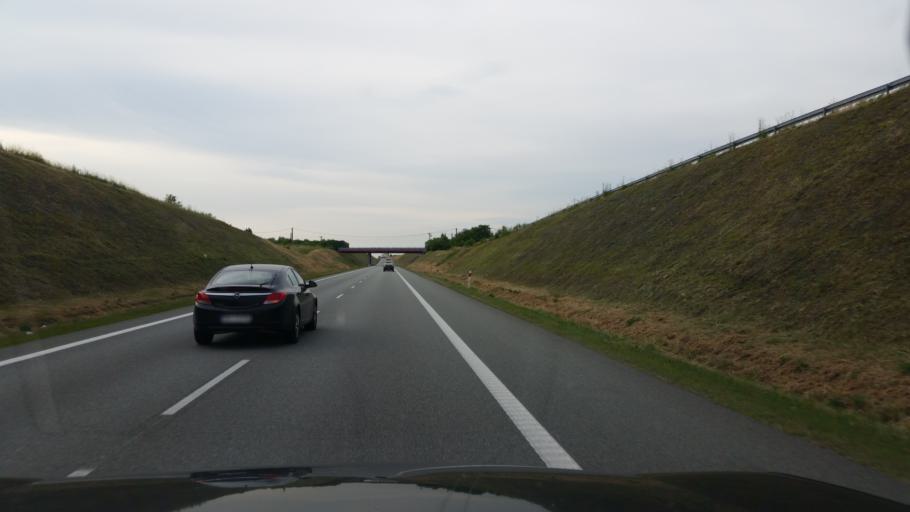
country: PL
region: Silesian Voivodeship
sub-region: Powiat bedzinski
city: Mierzecice
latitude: 50.4354
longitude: 19.1496
